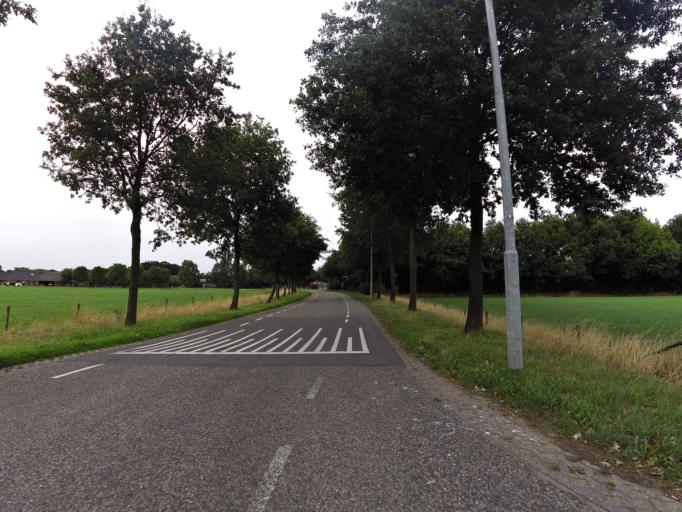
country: NL
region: Gelderland
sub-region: Gemeente Doesburg
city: Doesburg
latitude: 51.9927
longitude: 6.1423
